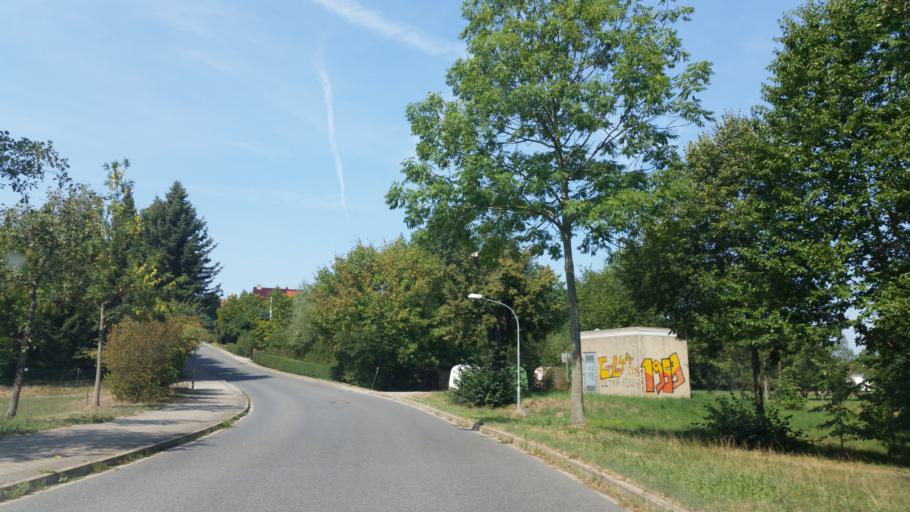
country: DE
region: Saxony
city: Klipphausen
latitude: 51.0708
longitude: 13.5309
